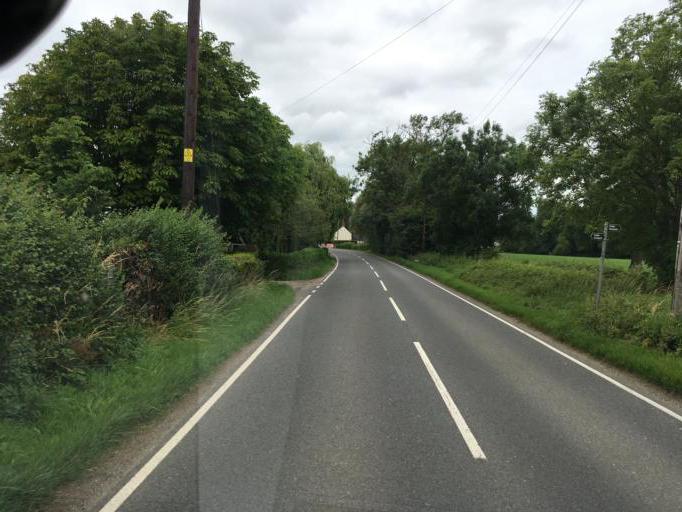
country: GB
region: England
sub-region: Gloucestershire
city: Stonehouse
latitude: 51.7326
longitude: -2.3158
